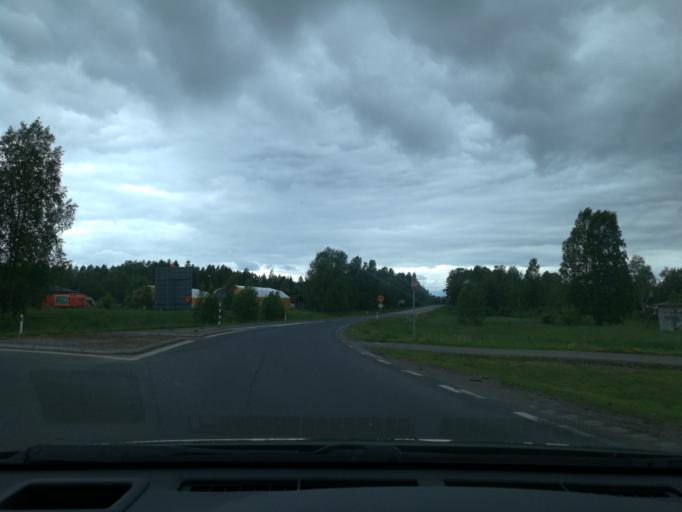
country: SE
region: Dalarna
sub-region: Smedjebackens Kommun
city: Smedjebacken
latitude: 60.1324
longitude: 15.4004
